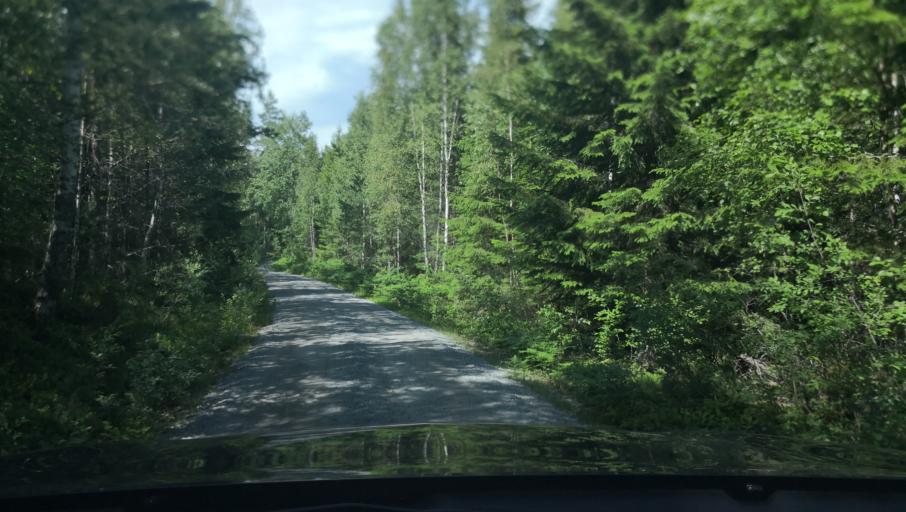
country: SE
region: Vaestmanland
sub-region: Surahammars Kommun
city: Ramnas
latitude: 59.9420
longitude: 16.1908
